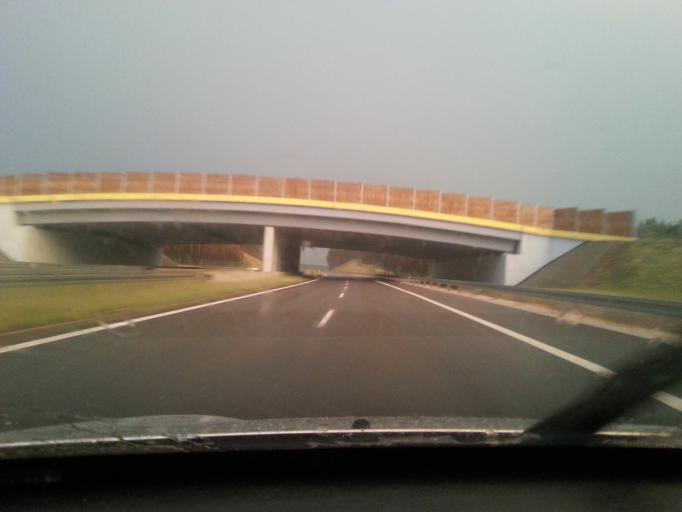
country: PL
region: Lodz Voivodeship
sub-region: Powiat pabianicki
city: Dobron
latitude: 51.6289
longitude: 19.2711
